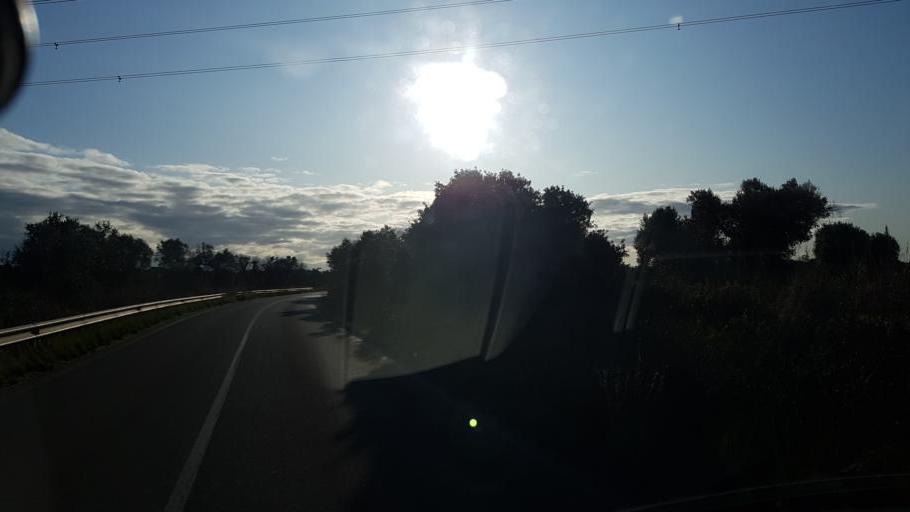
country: IT
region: Apulia
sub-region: Provincia di Brindisi
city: San Pietro Vernotico
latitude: 40.5548
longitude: 18.0307
